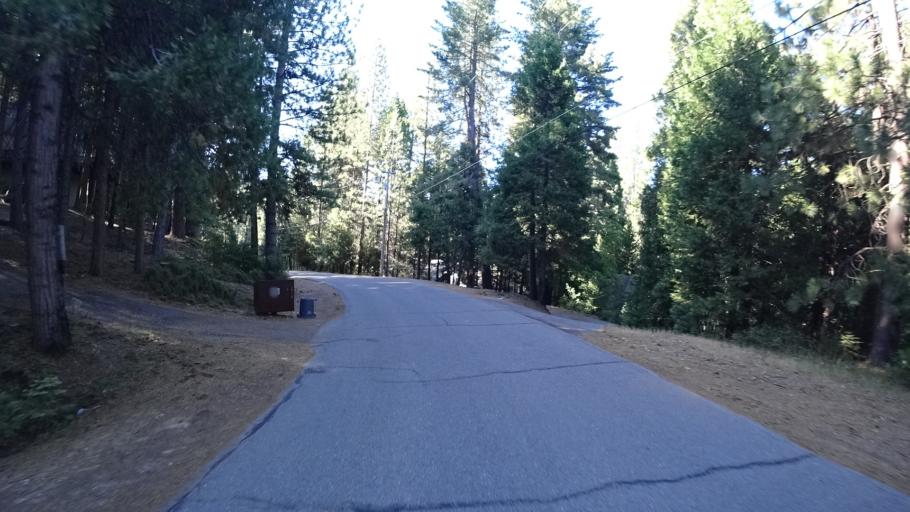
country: US
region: California
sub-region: Calaveras County
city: Arnold
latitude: 38.2568
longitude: -120.3216
